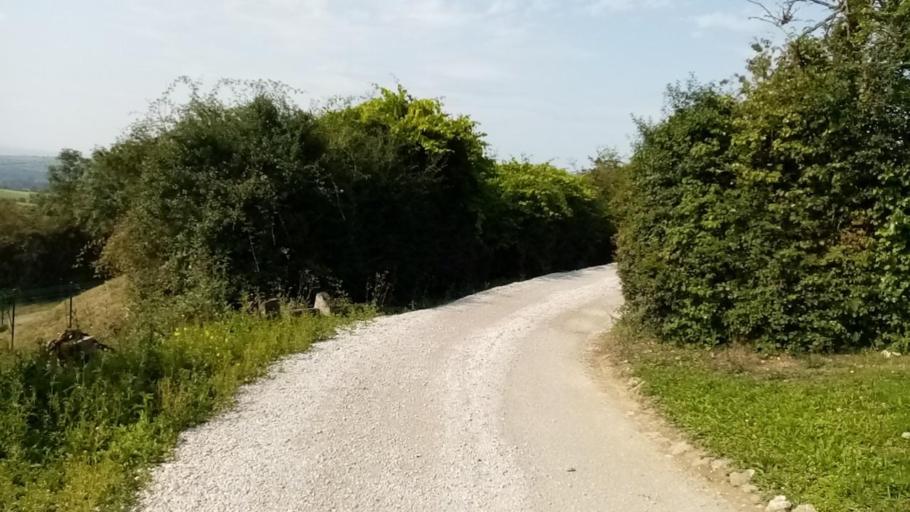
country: FR
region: Bourgogne
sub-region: Departement de Saone-et-Loire
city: Couches
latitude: 46.8994
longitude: 4.6125
